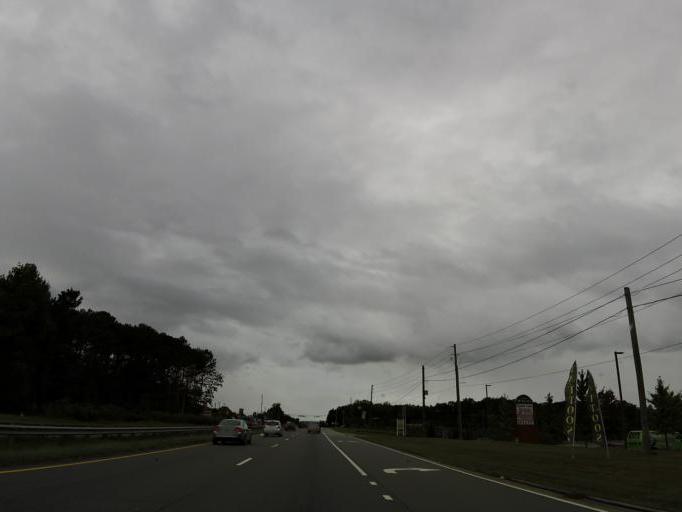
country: US
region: Georgia
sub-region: Cobb County
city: Kennesaw
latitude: 34.0285
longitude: -84.6462
